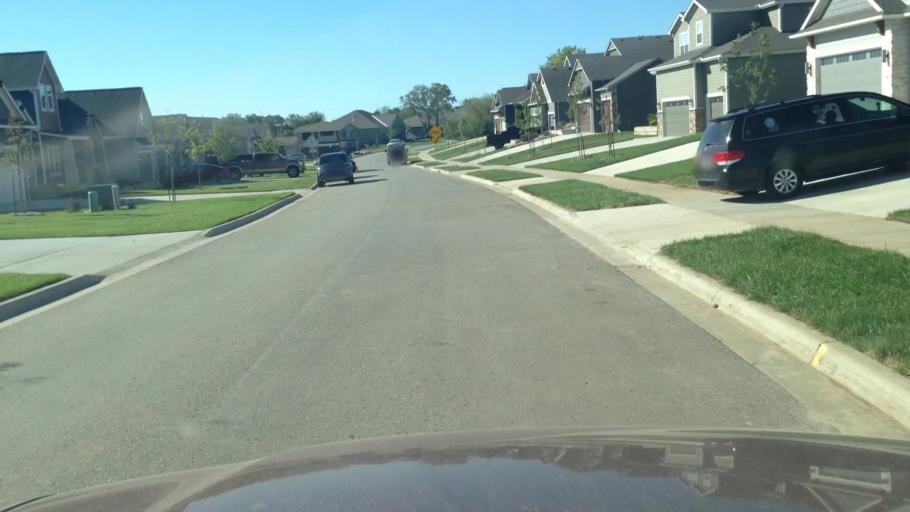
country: US
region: Kansas
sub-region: Douglas County
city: Lawrence
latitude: 38.9592
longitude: -95.3195
